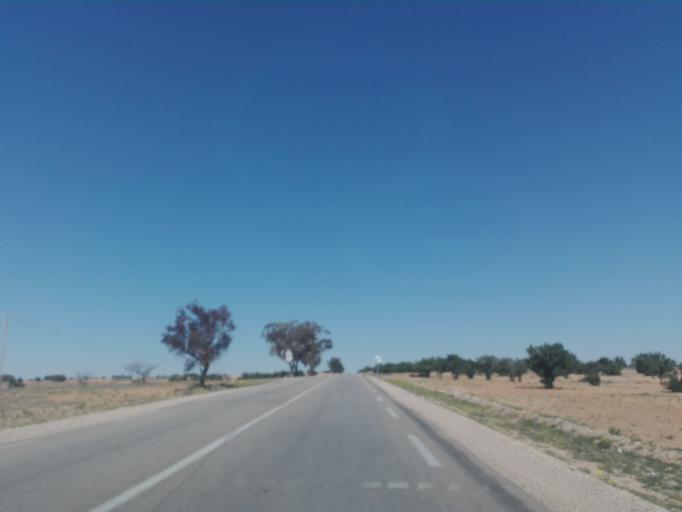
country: TN
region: Safaqis
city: Bi'r `Ali Bin Khalifah
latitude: 34.7473
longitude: 10.3546
